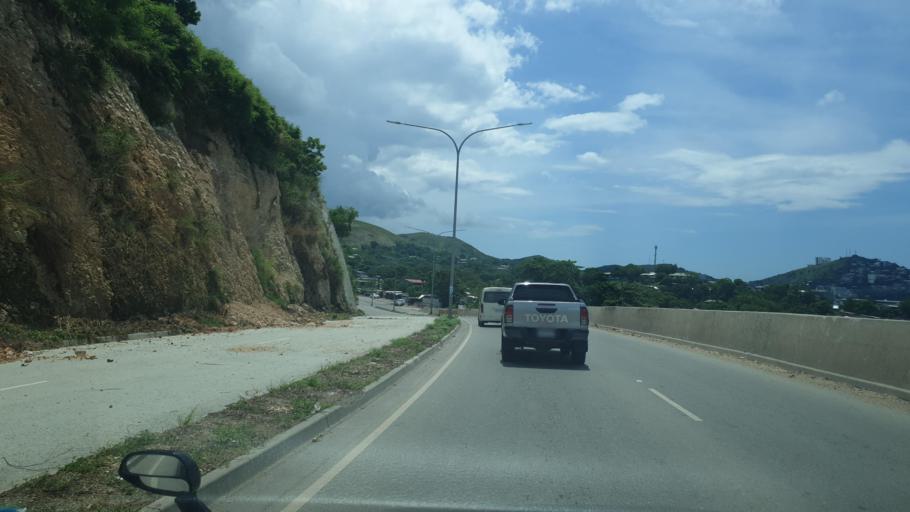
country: PG
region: National Capital
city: Port Moresby
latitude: -9.4488
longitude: 147.1489
